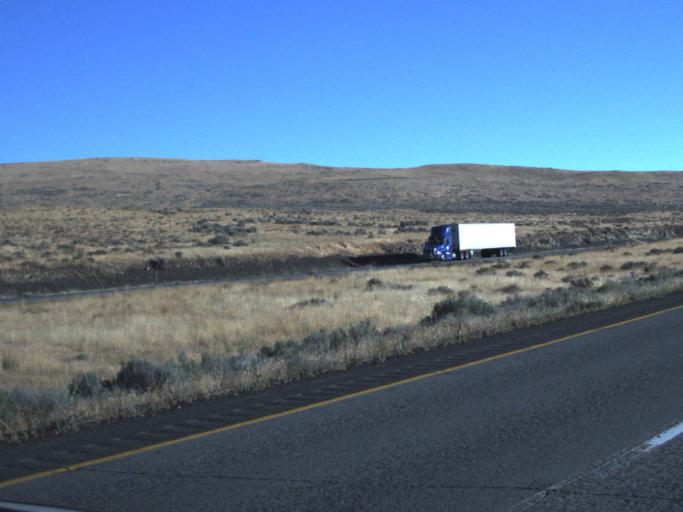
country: US
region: Washington
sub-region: Yakima County
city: Terrace Heights
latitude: 46.7162
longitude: -120.4106
